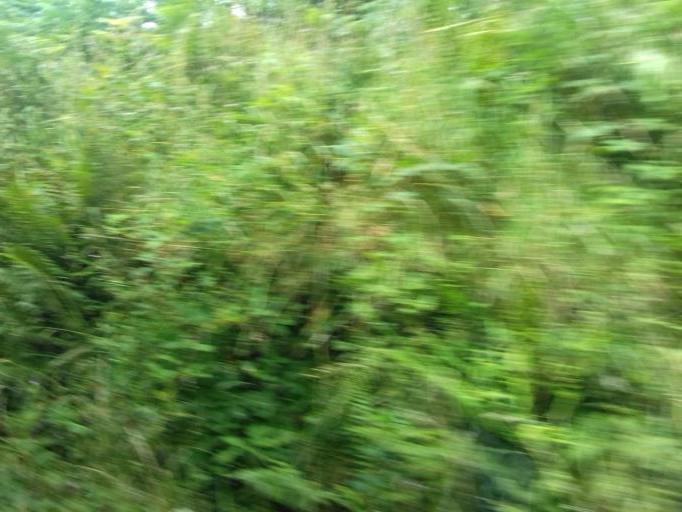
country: IE
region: Leinster
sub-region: County Carlow
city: Bagenalstown
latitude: 52.6294
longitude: -6.8192
